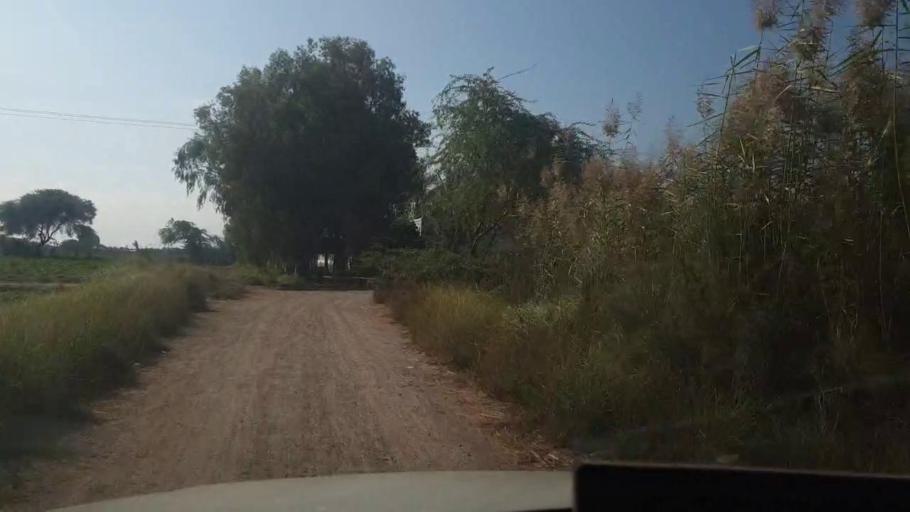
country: PK
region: Sindh
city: Mirpur Sakro
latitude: 24.4657
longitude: 67.5993
